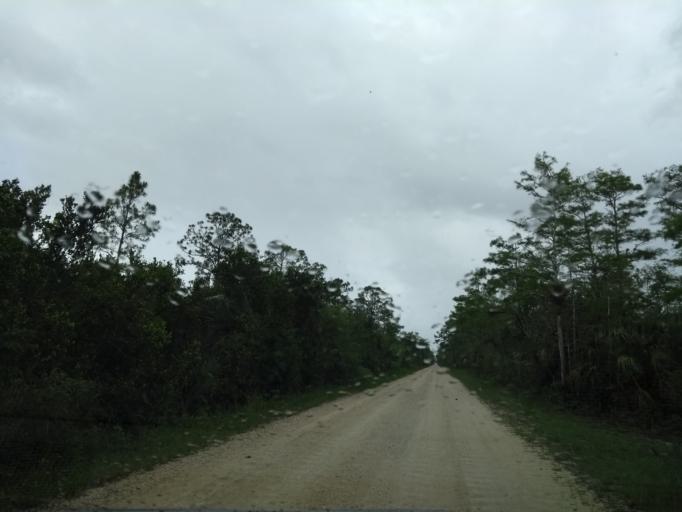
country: US
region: Florida
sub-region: Miami-Dade County
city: The Hammocks
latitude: 25.7605
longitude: -81.0024
